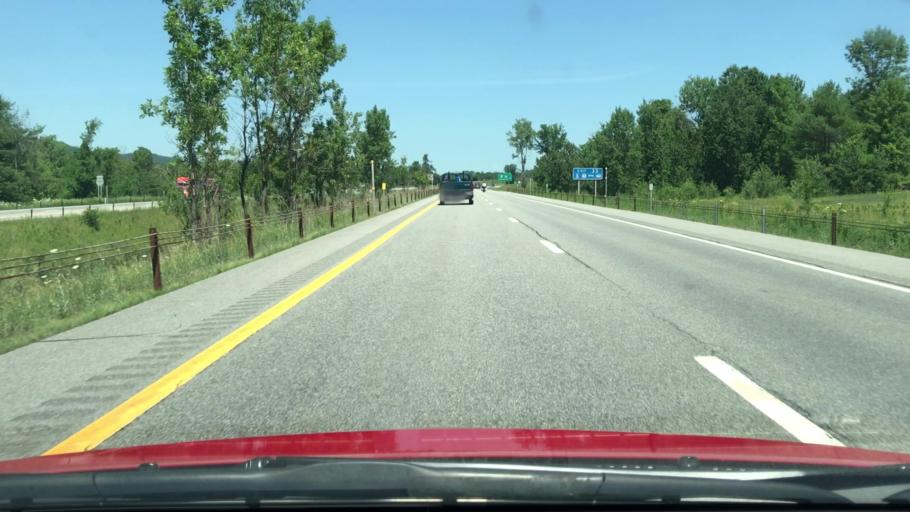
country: US
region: New York
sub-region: Essex County
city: Keeseville
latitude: 44.4358
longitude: -73.4917
